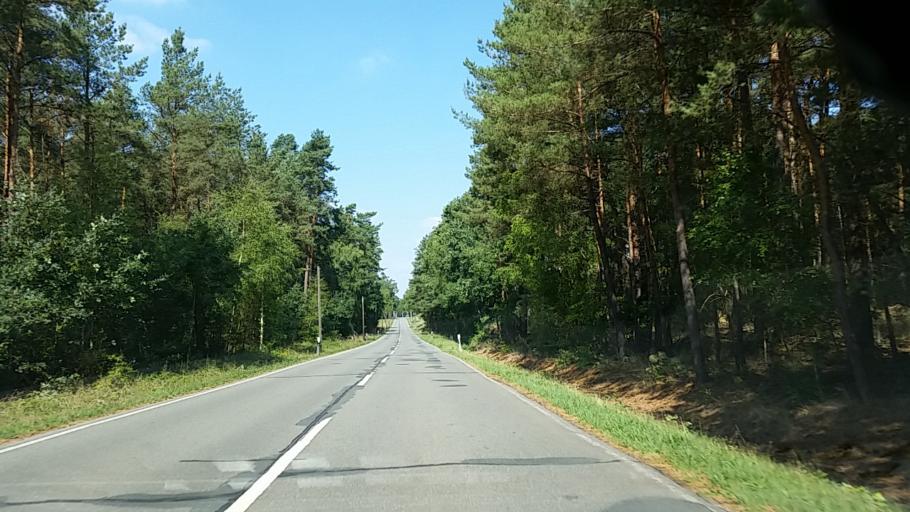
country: DE
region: Lower Saxony
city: Jelmstorf
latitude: 53.1226
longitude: 10.5374
